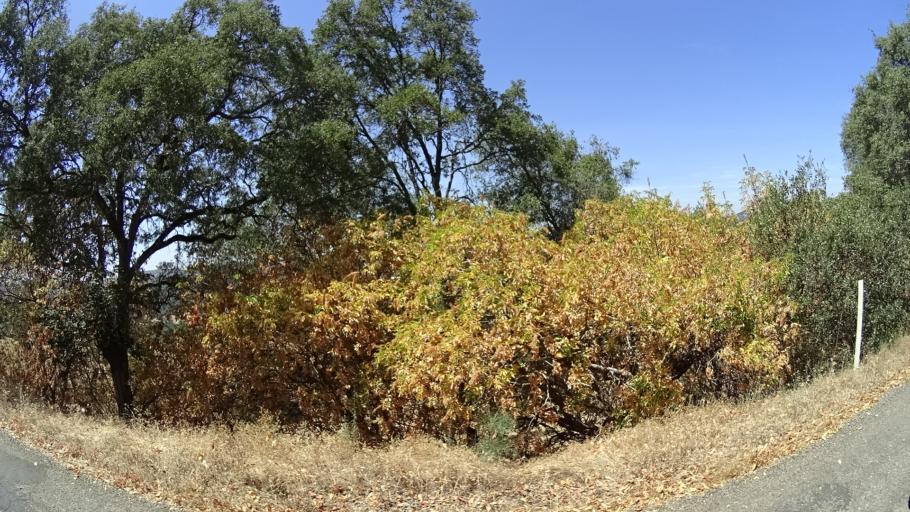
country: US
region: California
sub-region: Amador County
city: Jackson
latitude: 38.2916
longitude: -120.7161
